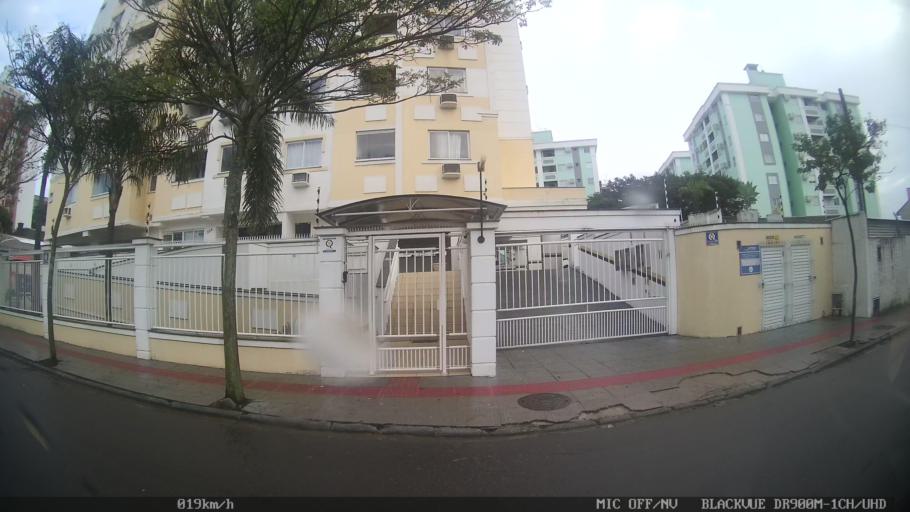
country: BR
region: Santa Catarina
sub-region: Sao Jose
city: Campinas
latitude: -27.5727
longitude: -48.6064
